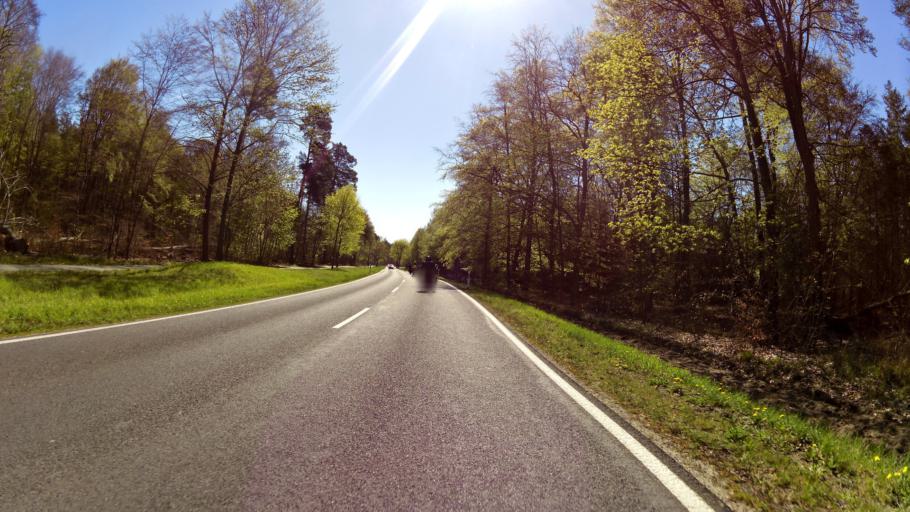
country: DE
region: Brandenburg
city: Bernau bei Berlin
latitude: 52.7161
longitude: 13.5266
